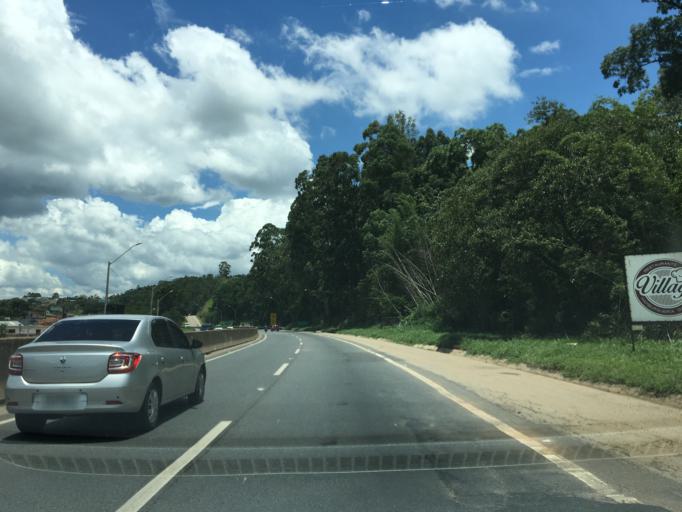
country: BR
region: Sao Paulo
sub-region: Mairipora
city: Mairipora
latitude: -23.2416
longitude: -46.5980
